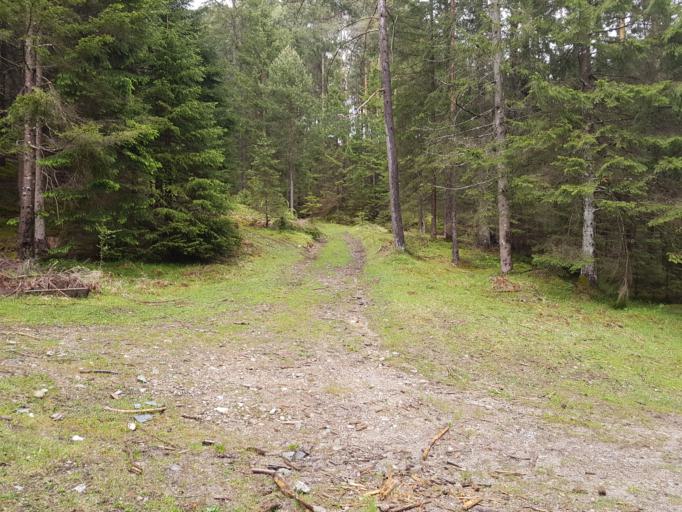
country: AT
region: Tyrol
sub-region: Politischer Bezirk Imst
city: Obsteig
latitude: 47.3059
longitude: 10.9156
